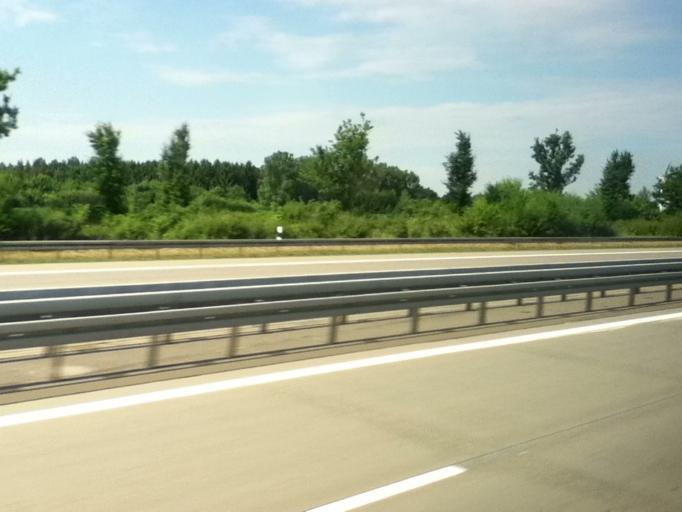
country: DE
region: Thuringia
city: Heyersdorf
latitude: 50.8363
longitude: 12.3696
